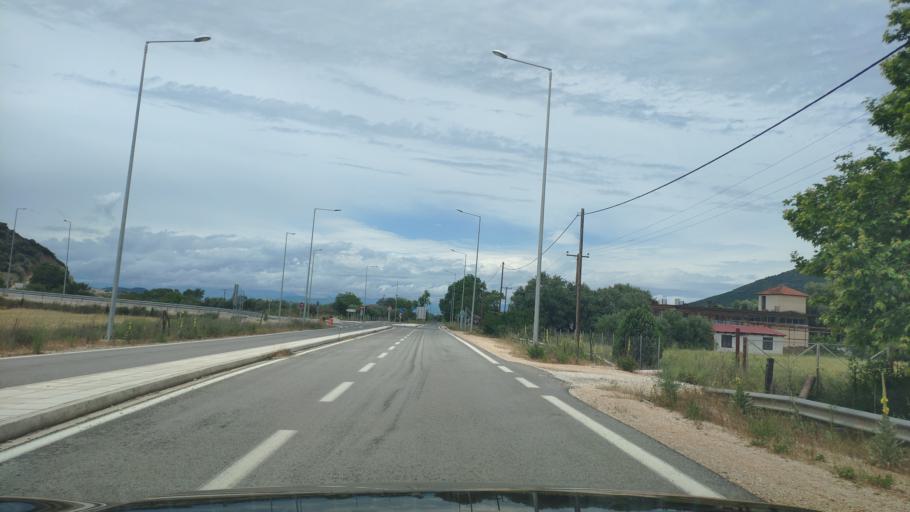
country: GR
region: West Greece
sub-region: Nomos Aitolias kai Akarnanias
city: Vonitsa
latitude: 38.8918
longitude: 20.9000
